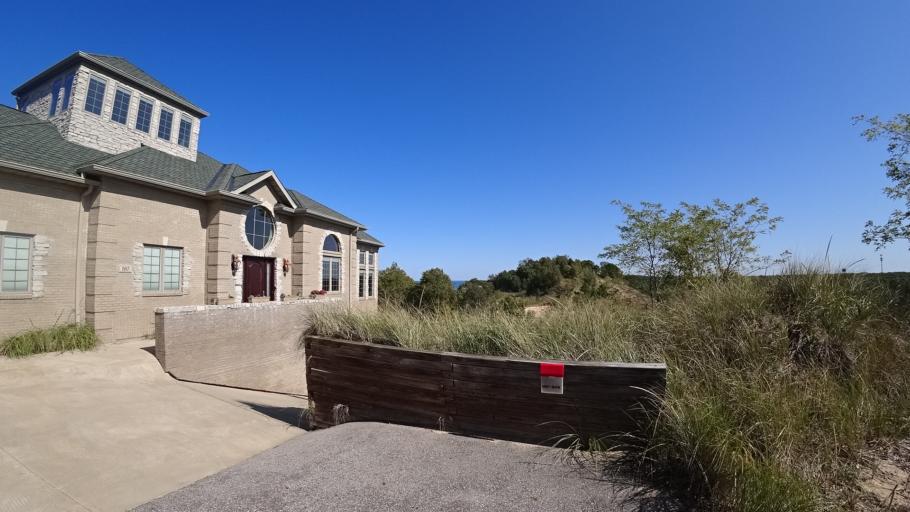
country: US
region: Indiana
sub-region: LaPorte County
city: Long Beach
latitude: 41.7336
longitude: -86.8797
